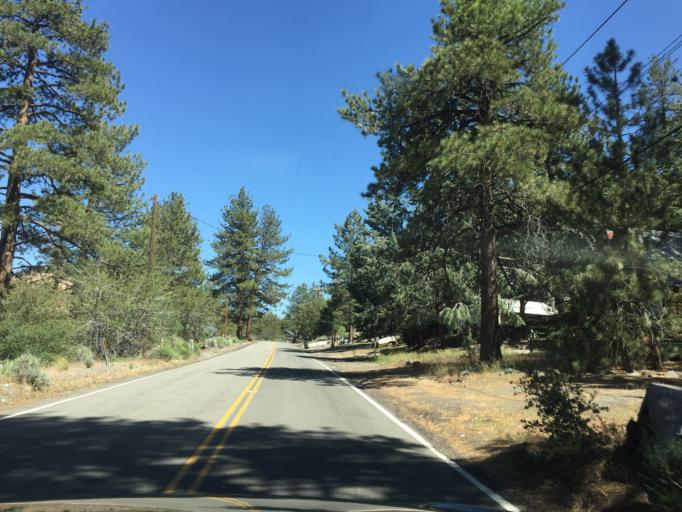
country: US
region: California
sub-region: San Bernardino County
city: Wrightwood
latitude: 34.3466
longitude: -117.6116
